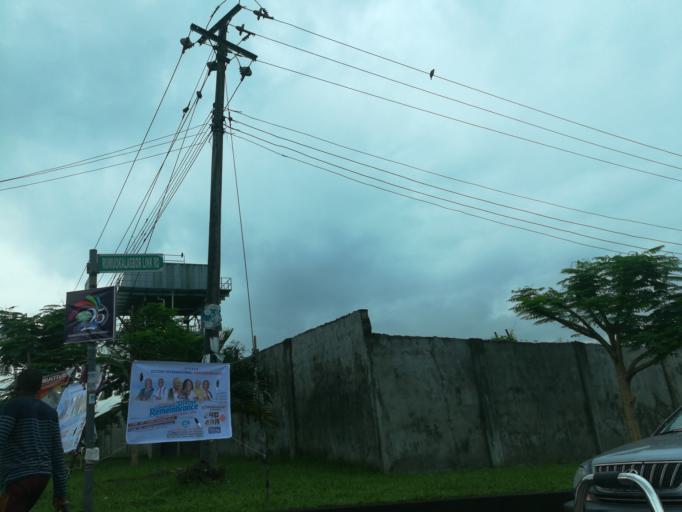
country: NG
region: Rivers
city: Port Harcourt
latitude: 4.8145
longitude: 7.0122
